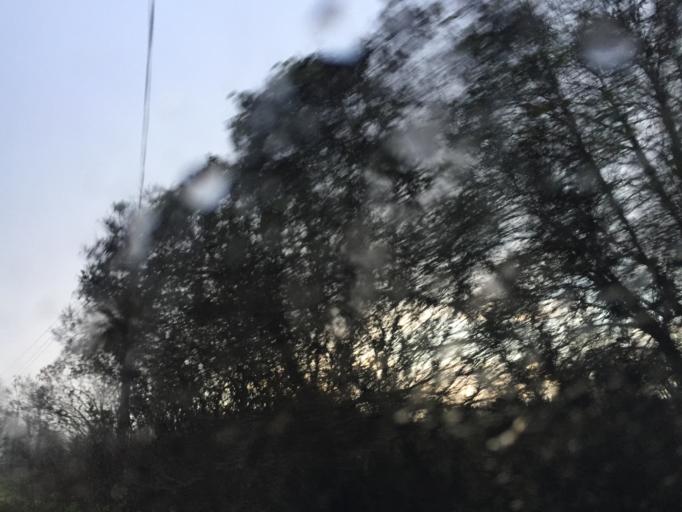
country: LV
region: Burtnieki
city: Matisi
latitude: 57.6859
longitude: 25.2481
